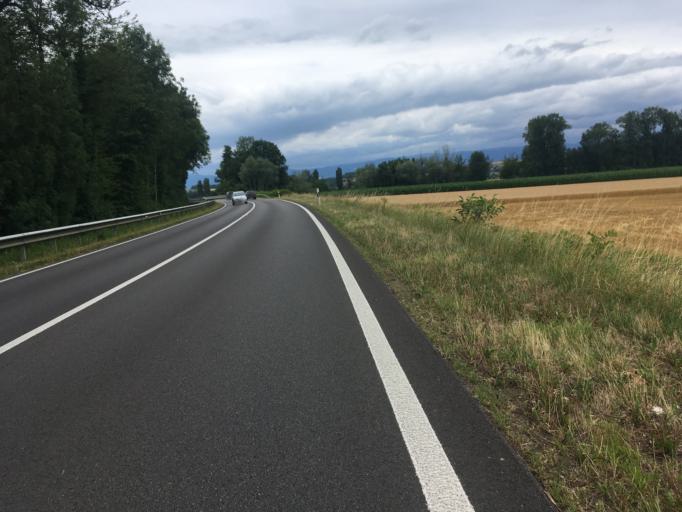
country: CH
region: Fribourg
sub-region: Broye District
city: Domdidier
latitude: 46.8883
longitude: 7.0184
